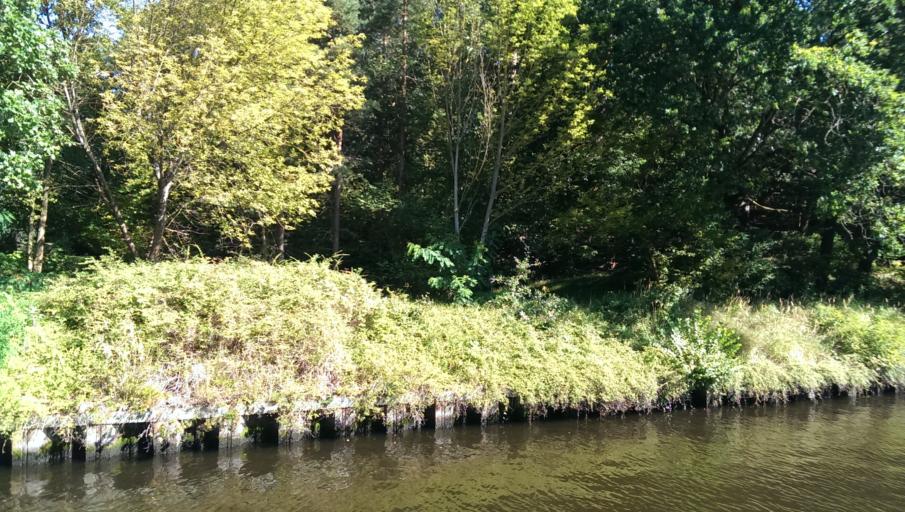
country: DE
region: Berlin
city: Wannsee
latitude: 52.3965
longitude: 13.1534
